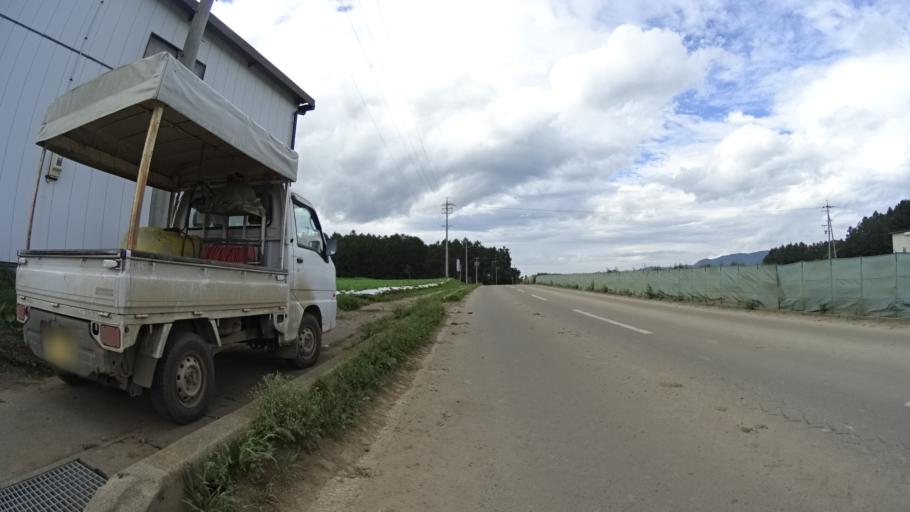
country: JP
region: Nagano
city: Saku
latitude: 35.9675
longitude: 138.5161
